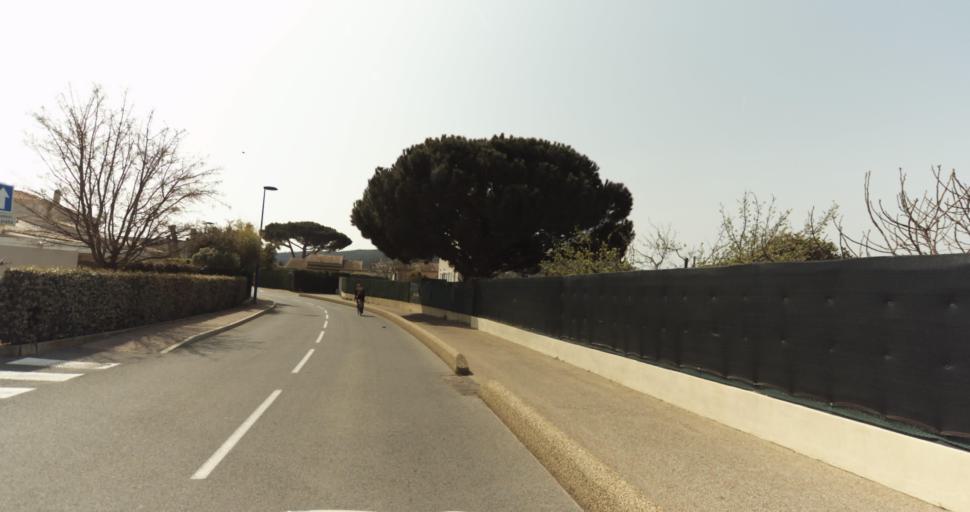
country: FR
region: Provence-Alpes-Cote d'Azur
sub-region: Departement du Var
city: Bormes-les-Mimosas
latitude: 43.1354
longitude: 6.3464
